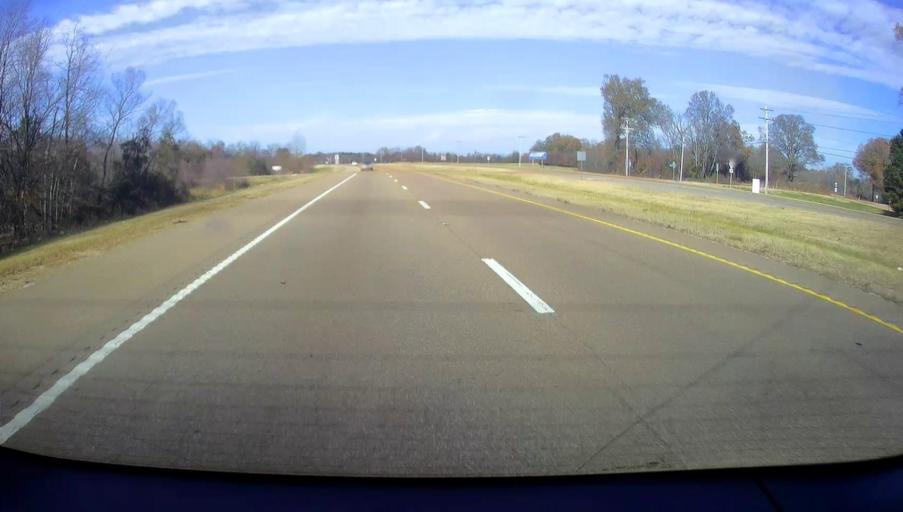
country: US
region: Tennessee
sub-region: Fayette County
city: Piperton
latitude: 34.9975
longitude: -89.6206
